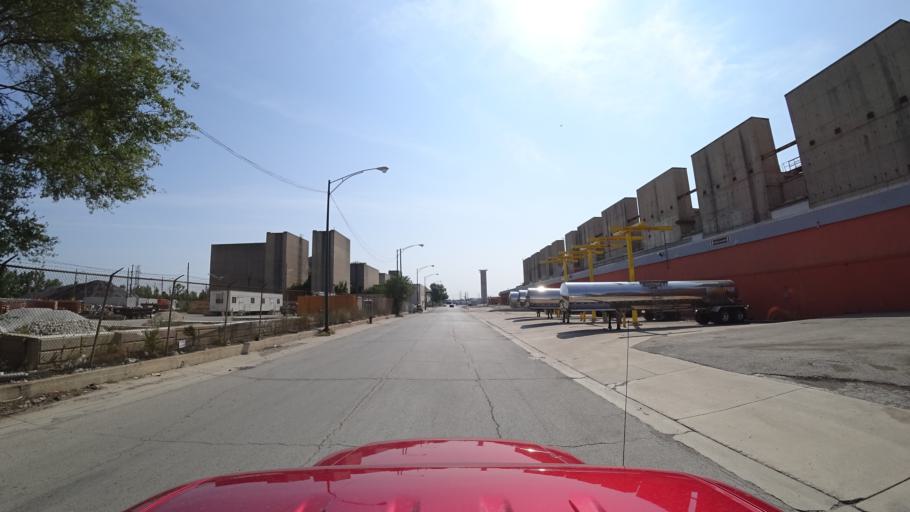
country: US
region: Illinois
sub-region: Cook County
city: Hometown
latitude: 41.7622
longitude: -87.7385
